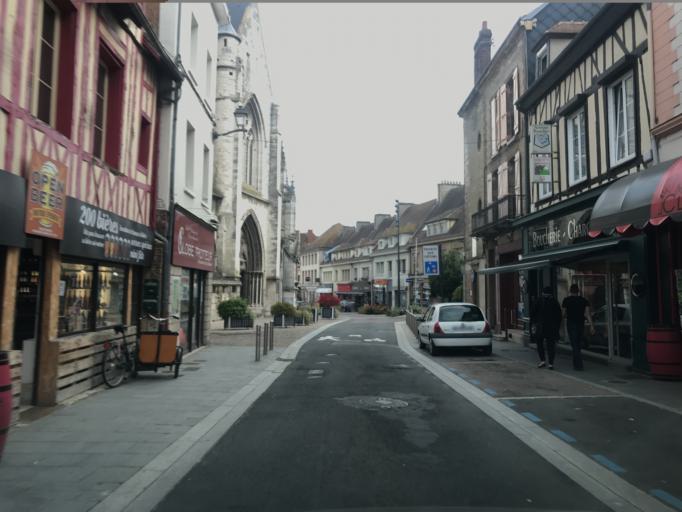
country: FR
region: Haute-Normandie
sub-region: Departement de l'Eure
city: Louviers
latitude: 49.2134
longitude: 1.1695
